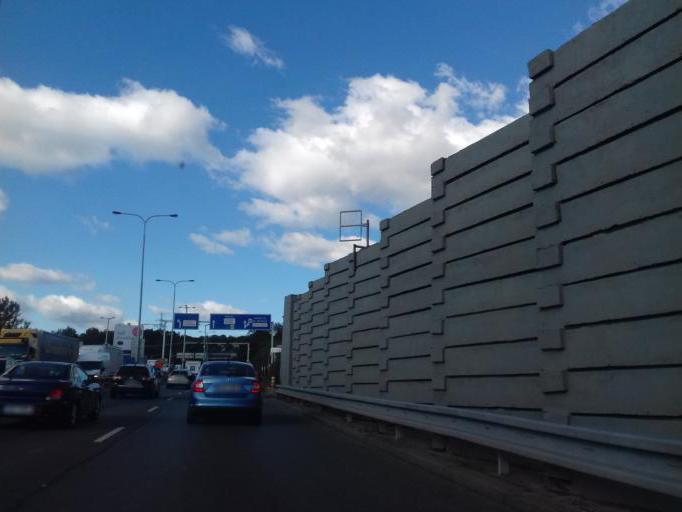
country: CZ
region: Praha
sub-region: Praha 9
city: Vysocany
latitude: 50.1084
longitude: 14.5316
